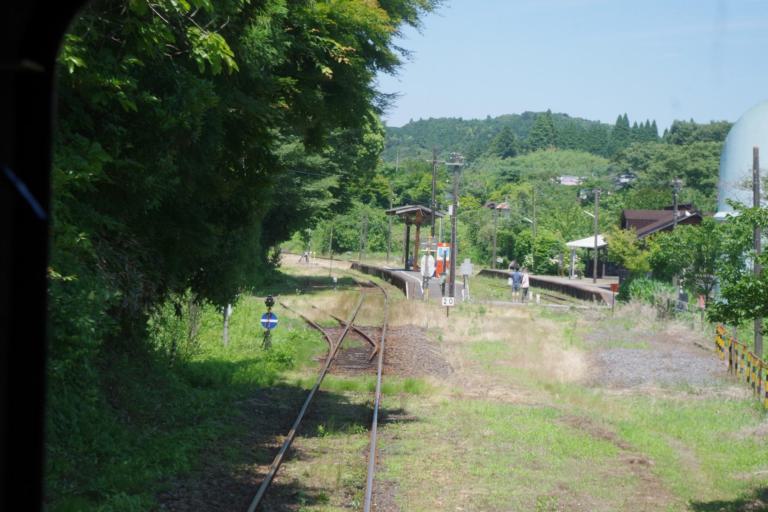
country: JP
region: Chiba
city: Katsuura
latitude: 35.2496
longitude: 140.2005
